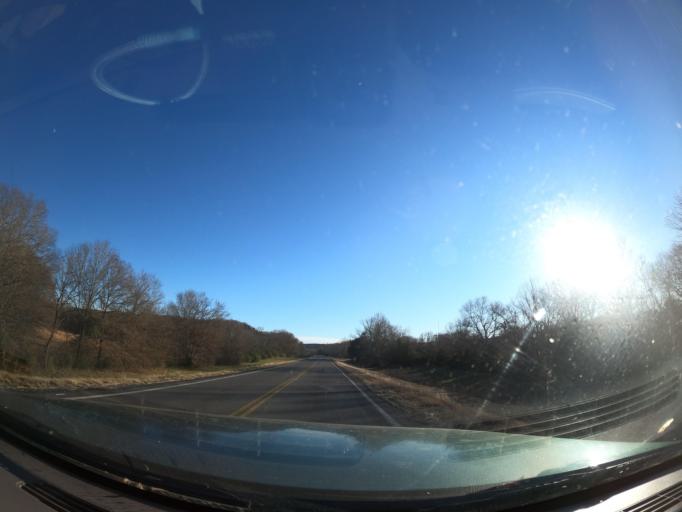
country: US
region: Oklahoma
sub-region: Latimer County
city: Wilburton
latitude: 34.9411
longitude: -95.3413
